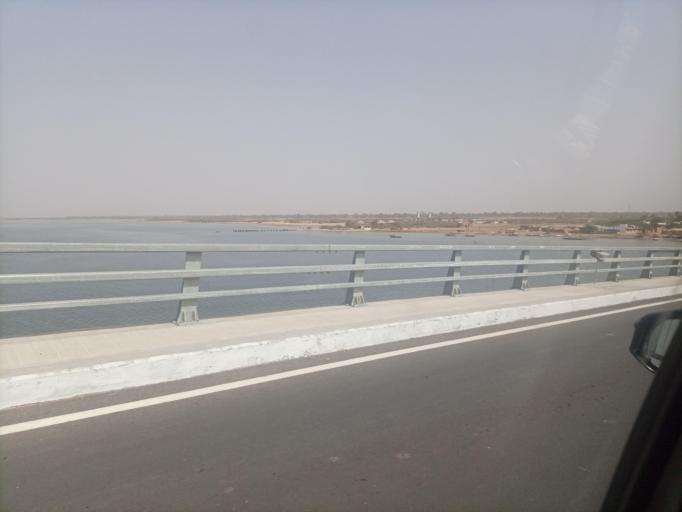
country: SN
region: Fatick
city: Foundiougne
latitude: 14.1326
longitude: -16.4673
